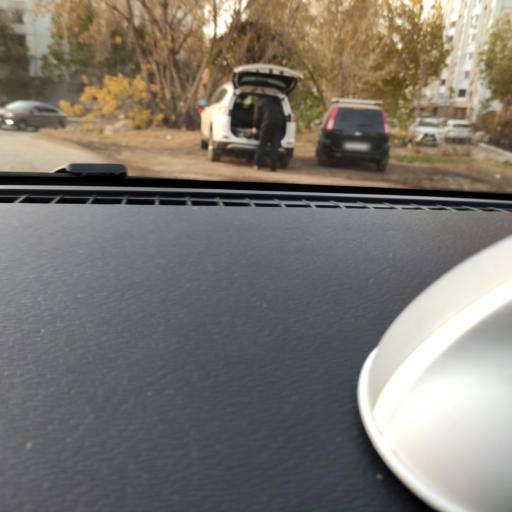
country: RU
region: Samara
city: Samara
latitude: 53.1967
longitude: 50.1470
